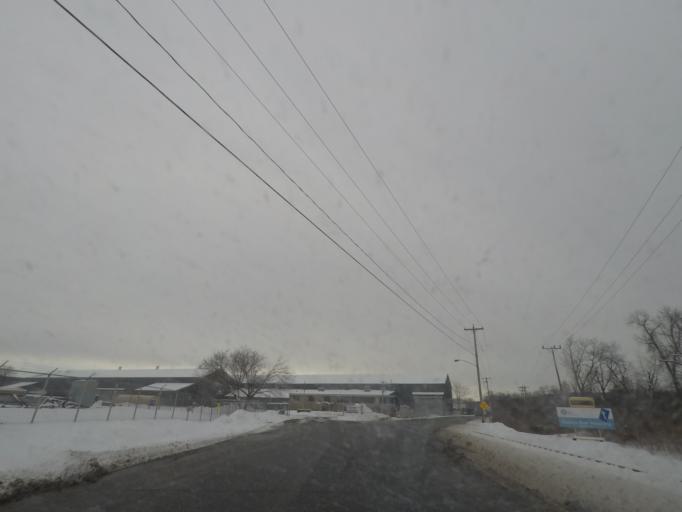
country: US
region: New York
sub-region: Rensselaer County
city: Rensselaer
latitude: 42.6153
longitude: -73.7644
